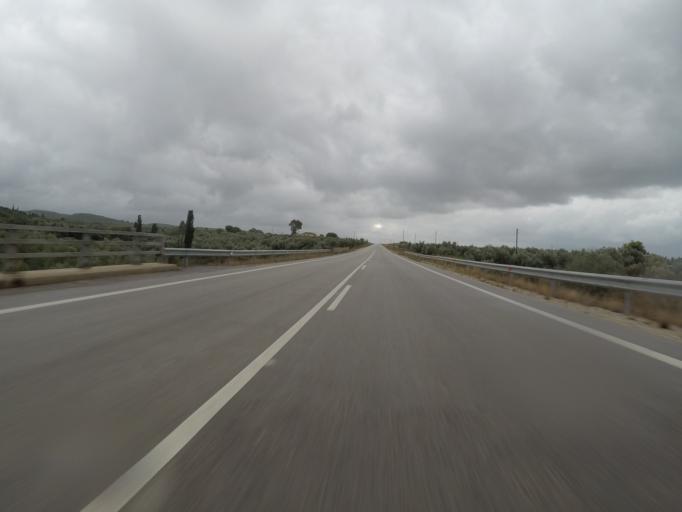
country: GR
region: Peloponnese
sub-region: Nomos Messinias
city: Gargalianoi
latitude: 37.0203
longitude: 21.6385
